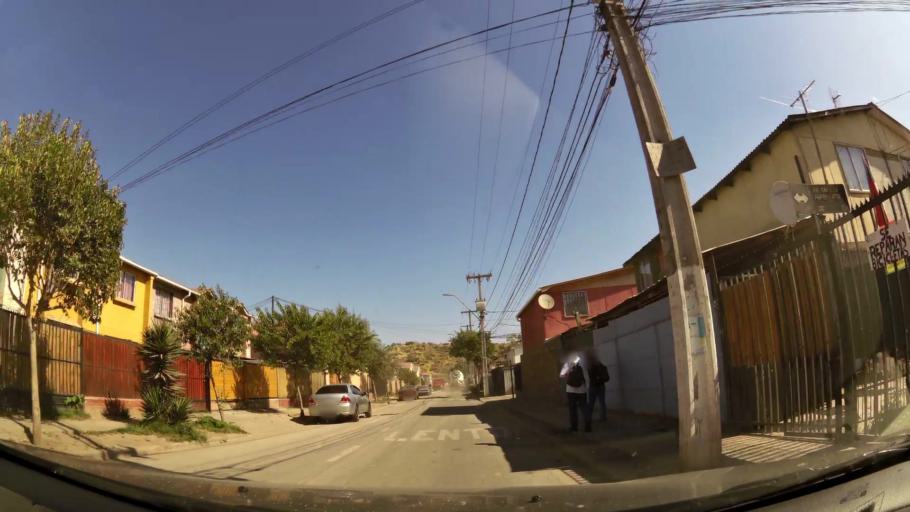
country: CL
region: Santiago Metropolitan
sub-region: Provincia de Maipo
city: San Bernardo
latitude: -33.6153
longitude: -70.7089
